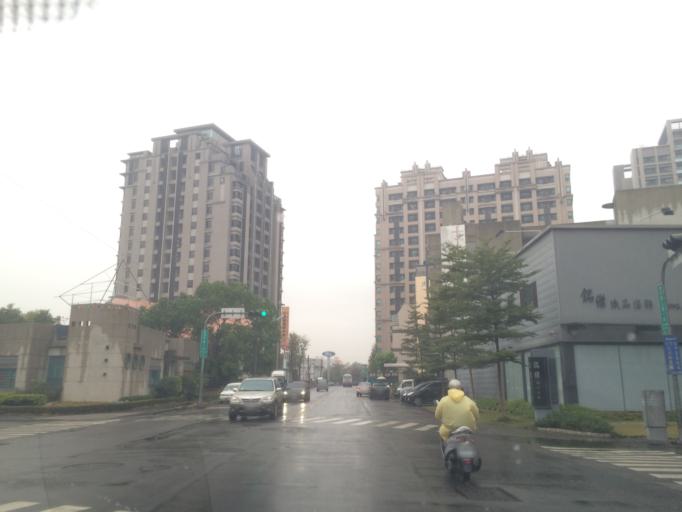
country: TW
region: Taiwan
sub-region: Taichung City
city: Taichung
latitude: 24.1835
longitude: 120.6877
